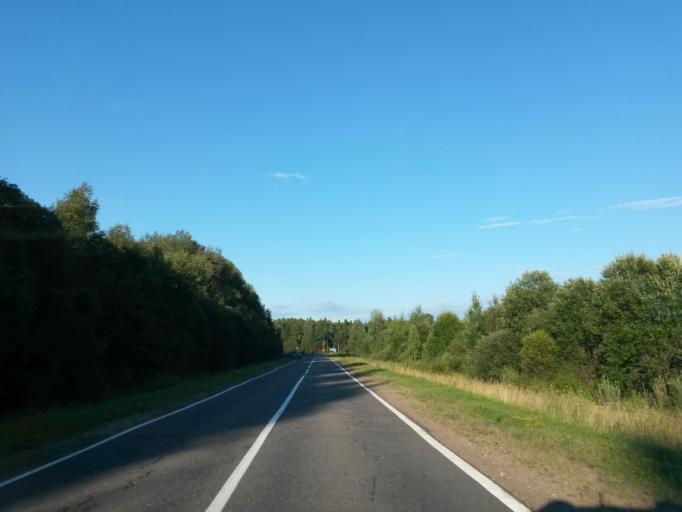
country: RU
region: Jaroslavl
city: Tutayev
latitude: 57.9484
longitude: 39.4922
